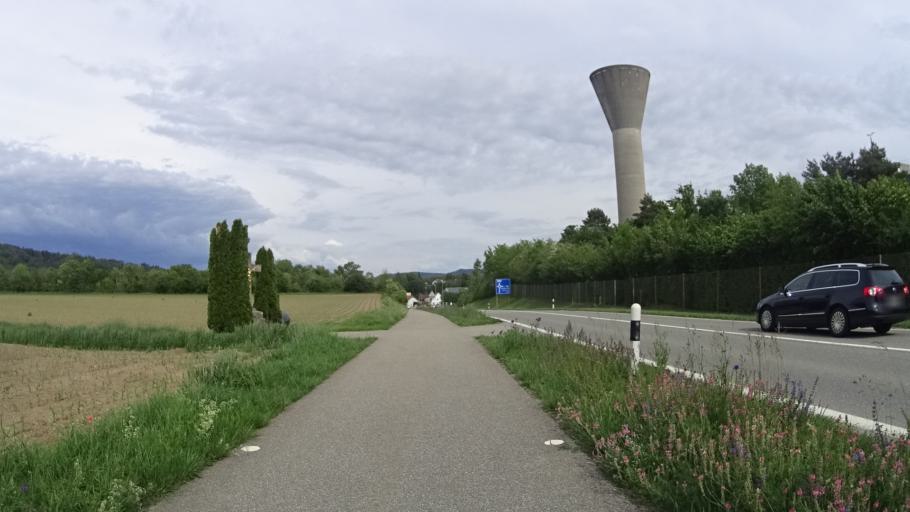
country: CH
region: Aargau
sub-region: Bezirk Laufenburg
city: Eiken
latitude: 47.5519
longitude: 7.9804
